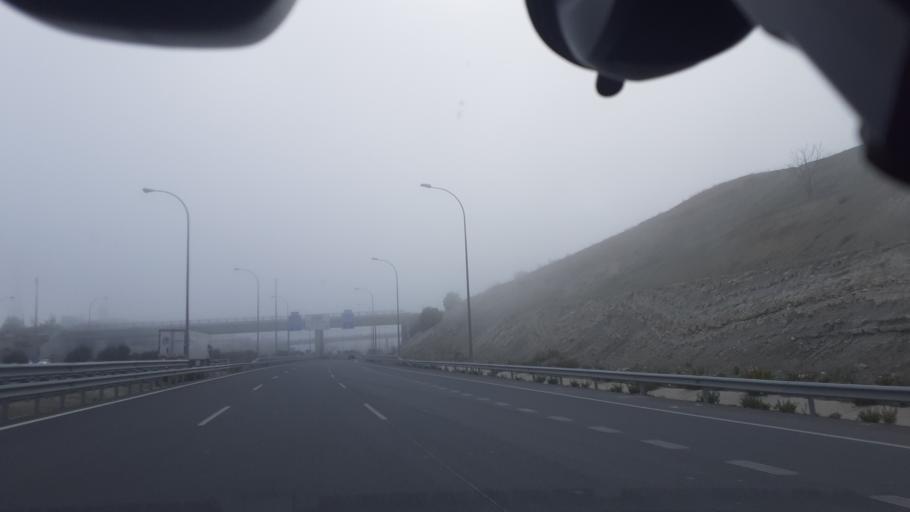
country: ES
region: Madrid
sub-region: Provincia de Madrid
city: Villa de Vallecas
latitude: 40.3797
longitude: -3.5904
